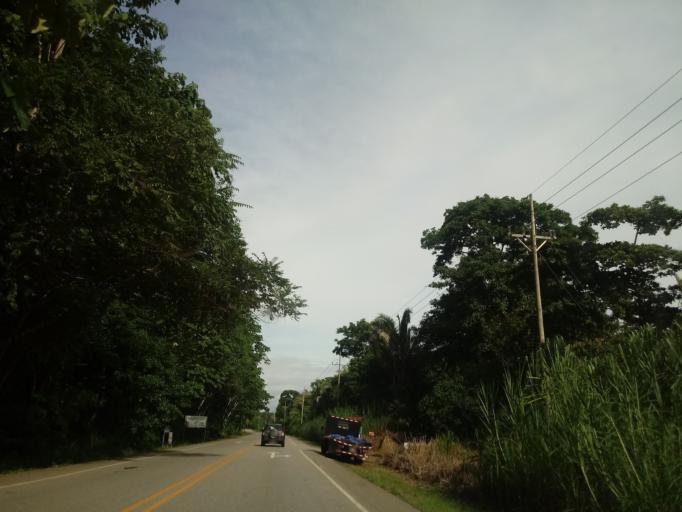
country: CR
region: San Jose
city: Daniel Flores
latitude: 9.1942
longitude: -83.7798
